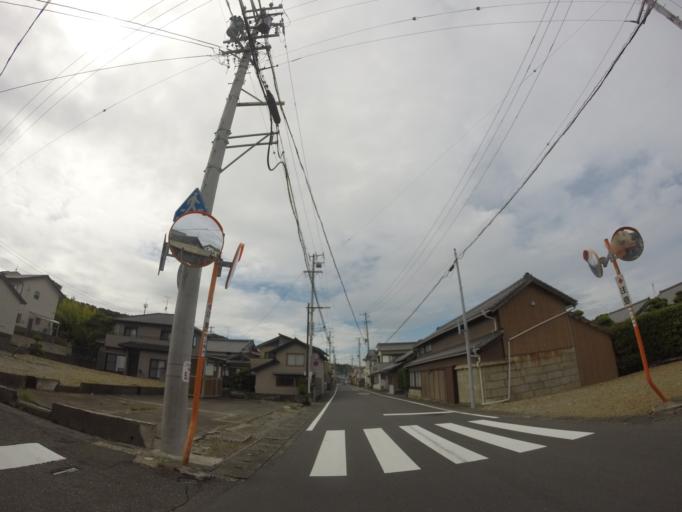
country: JP
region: Shizuoka
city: Oyama
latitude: 34.6314
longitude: 138.1953
